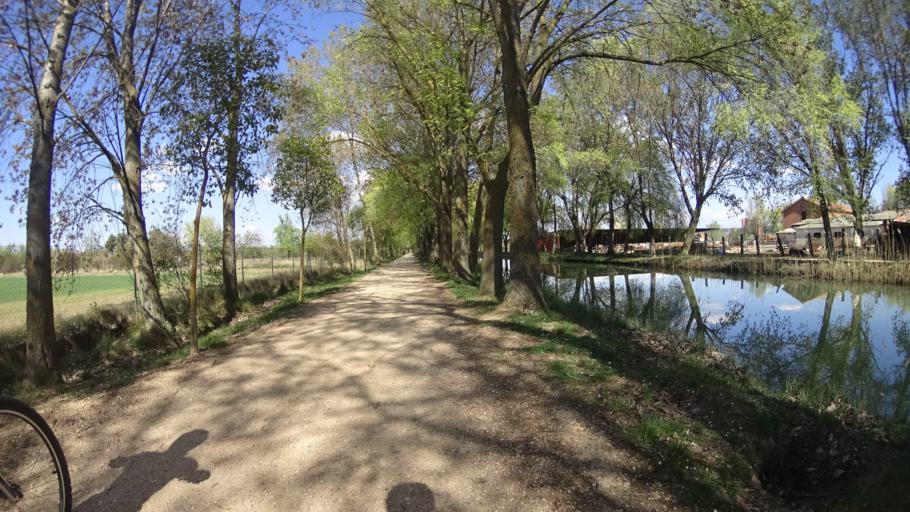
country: ES
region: Castille and Leon
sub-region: Provincia de Palencia
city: Palencia
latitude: 42.0023
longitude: -4.5501
